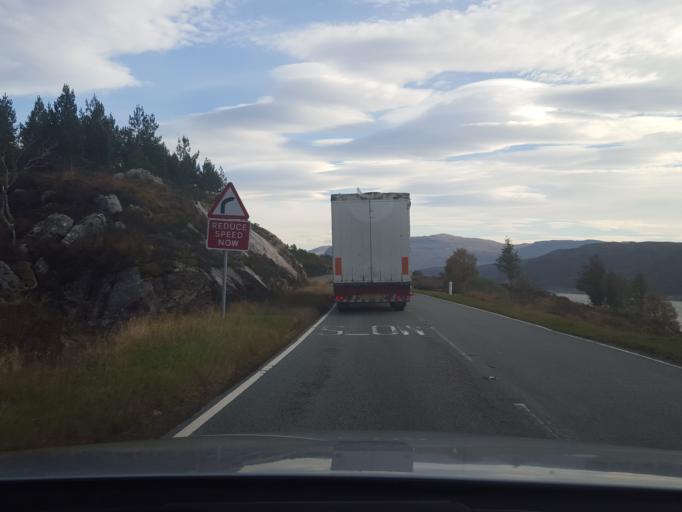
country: GB
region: Scotland
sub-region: Highland
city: Spean Bridge
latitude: 57.1497
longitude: -5.0349
